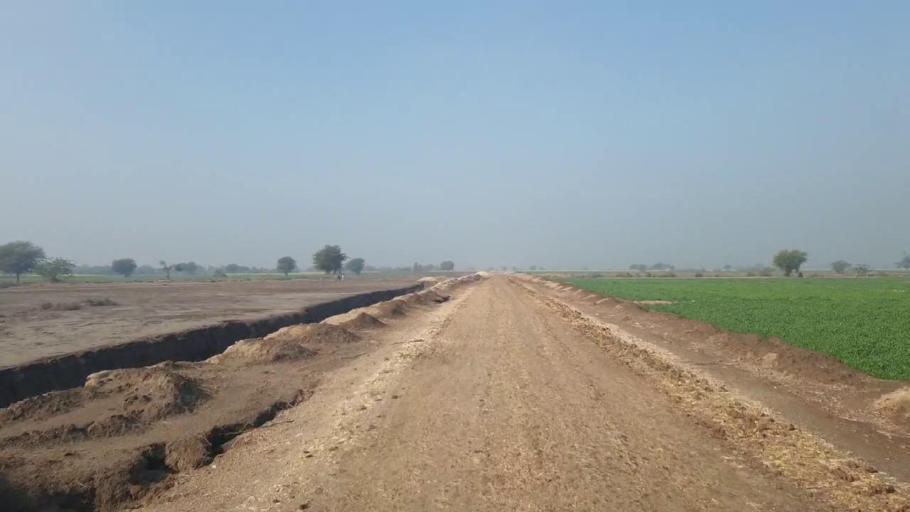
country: PK
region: Sindh
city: Shahdadpur
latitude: 25.9509
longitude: 68.5757
